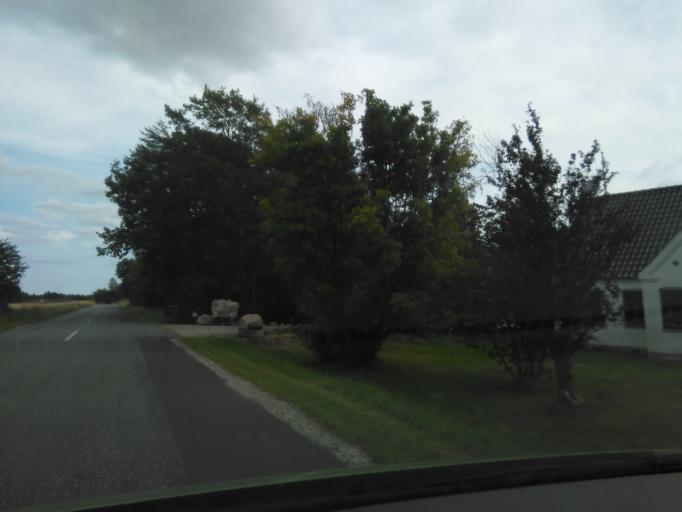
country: DK
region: Central Jutland
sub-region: Arhus Kommune
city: Marslet
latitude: 56.0413
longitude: 10.1696
